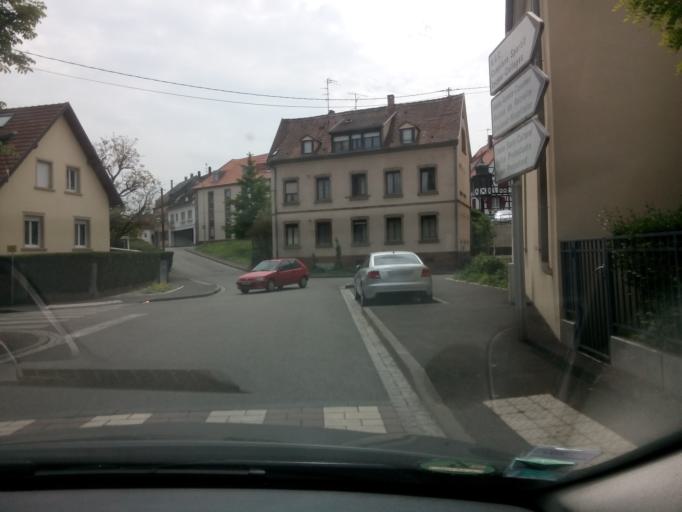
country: FR
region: Alsace
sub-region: Departement du Bas-Rhin
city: Bischwiller
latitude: 48.7688
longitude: 7.8631
